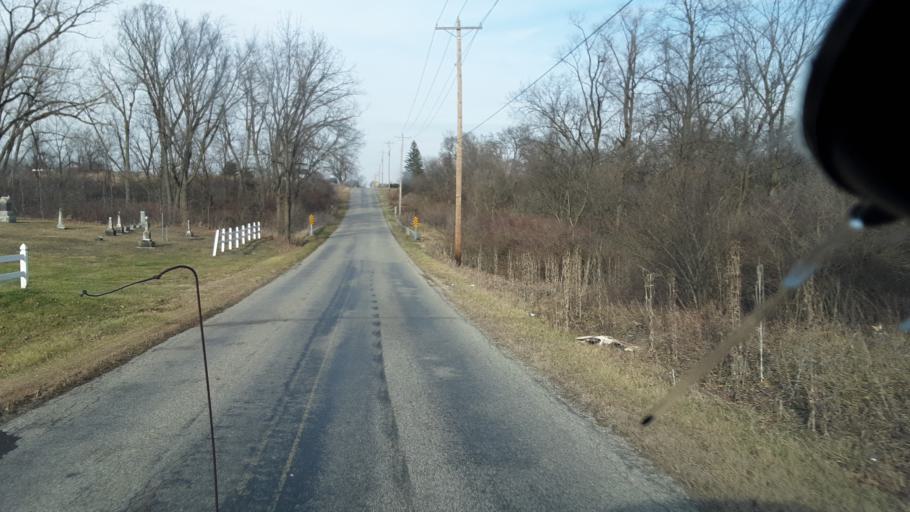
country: US
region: Indiana
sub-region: DeKalb County
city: Butler
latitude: 41.3944
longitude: -84.8891
